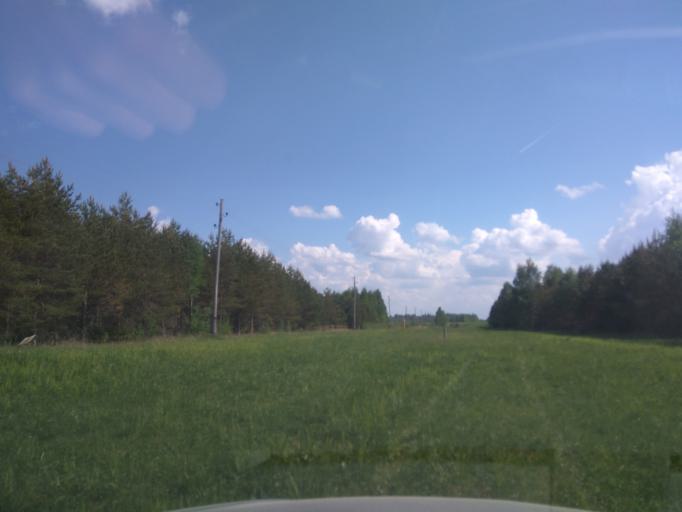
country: LV
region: Kuldigas Rajons
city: Kuldiga
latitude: 57.1804
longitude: 22.0033
